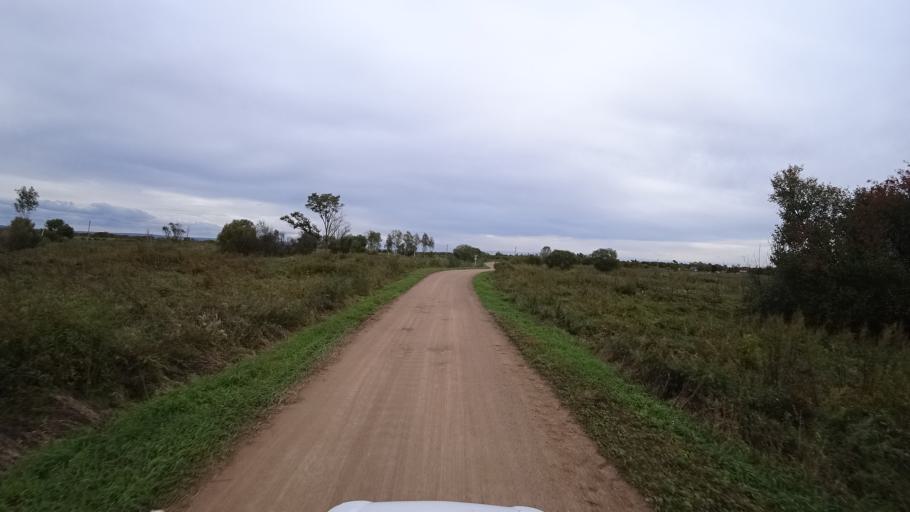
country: RU
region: Amur
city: Arkhara
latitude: 49.4369
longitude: 130.2581
